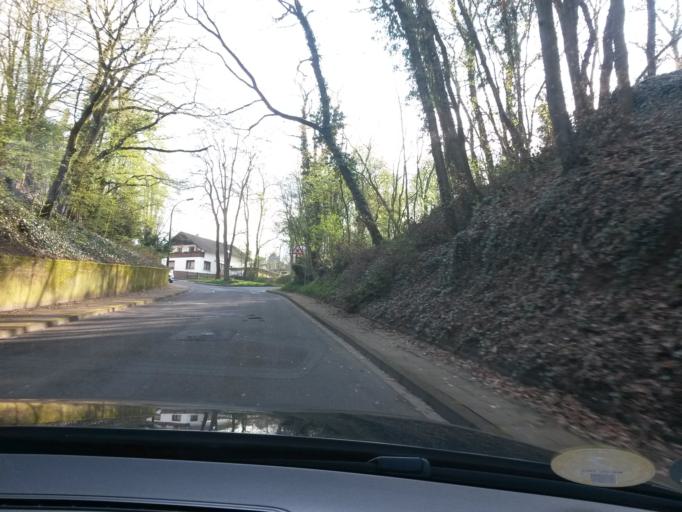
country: DE
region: North Rhine-Westphalia
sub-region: Regierungsbezirk Koln
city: Alfter
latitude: 50.7087
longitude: 7.0378
